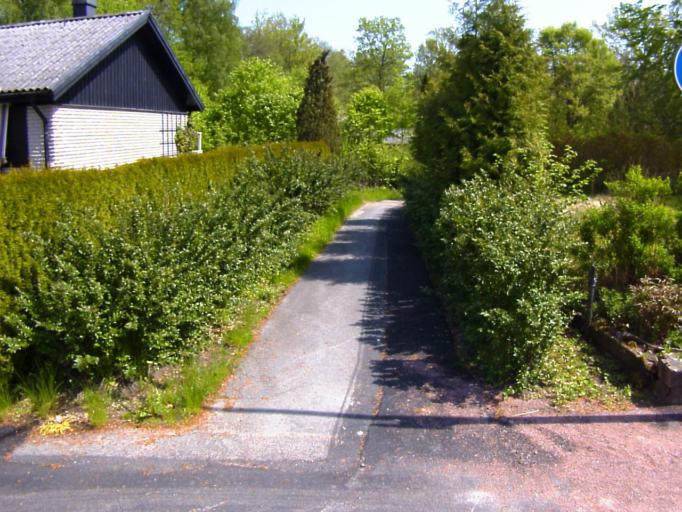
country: SE
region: Skane
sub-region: Kristianstads Kommun
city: Tollarp
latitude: 56.1731
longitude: 14.2936
